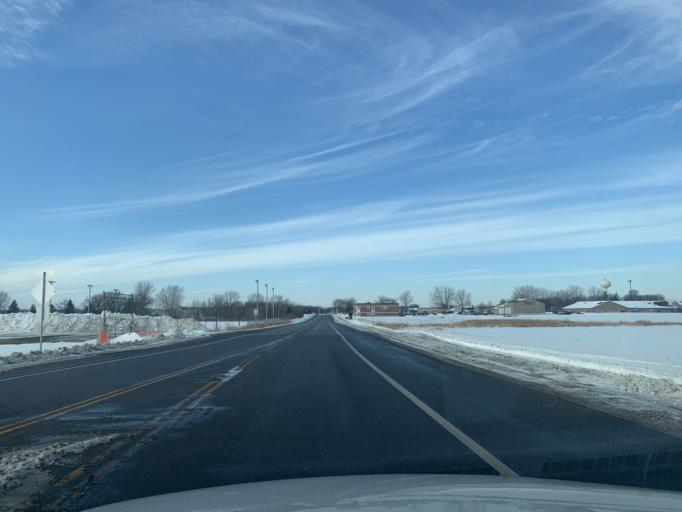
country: US
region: Minnesota
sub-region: Wright County
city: Buffalo
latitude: 45.1656
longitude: -93.8489
